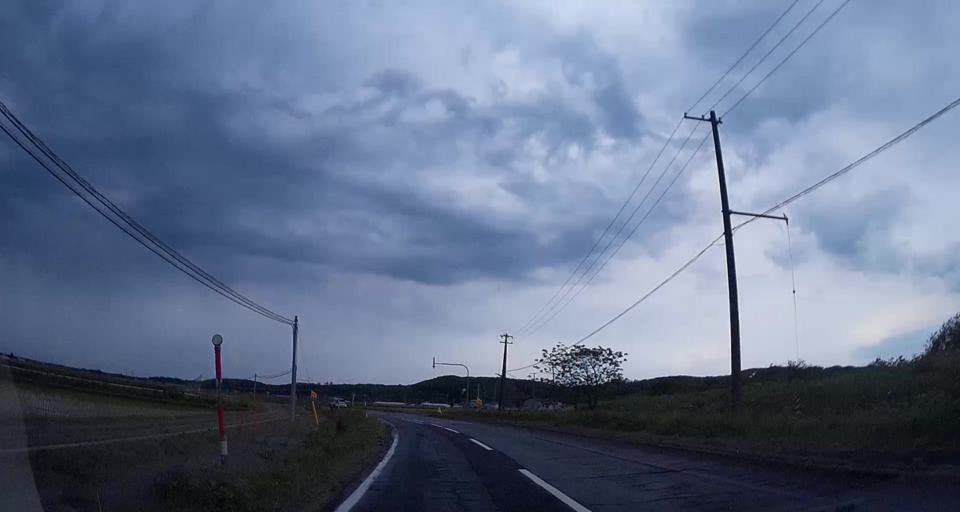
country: JP
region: Hokkaido
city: Chitose
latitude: 42.7194
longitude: 141.8716
